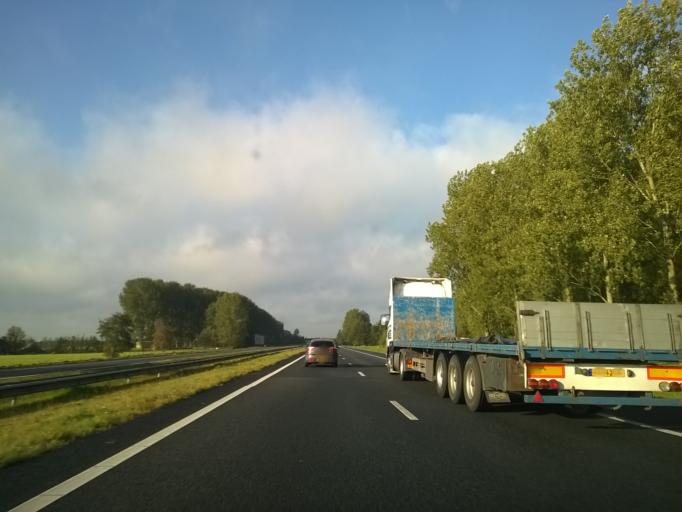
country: NL
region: Groningen
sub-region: Gemeente Grootegast
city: Grootegast
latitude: 53.1662
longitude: 6.3101
